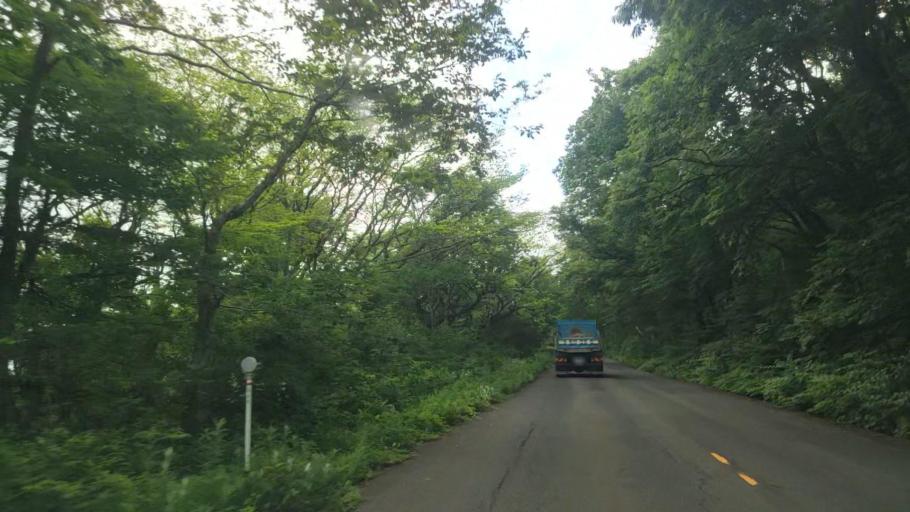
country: JP
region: Tottori
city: Yonago
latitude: 35.3809
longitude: 133.5222
